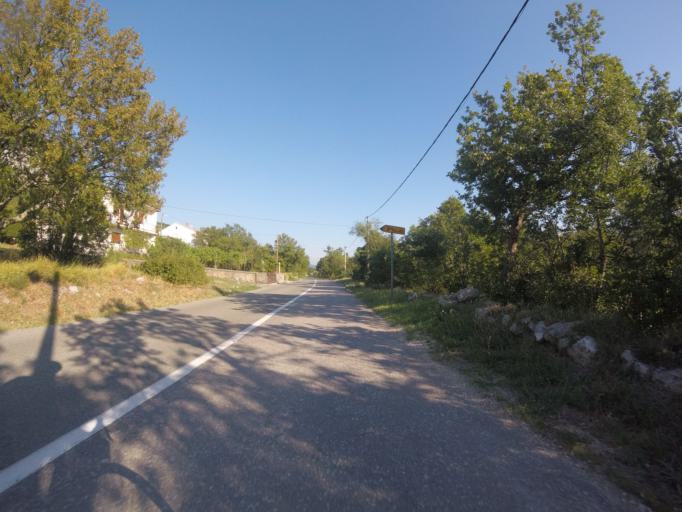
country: HR
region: Primorsko-Goranska
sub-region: Grad Crikvenica
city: Jadranovo
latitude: 45.2349
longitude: 14.6601
